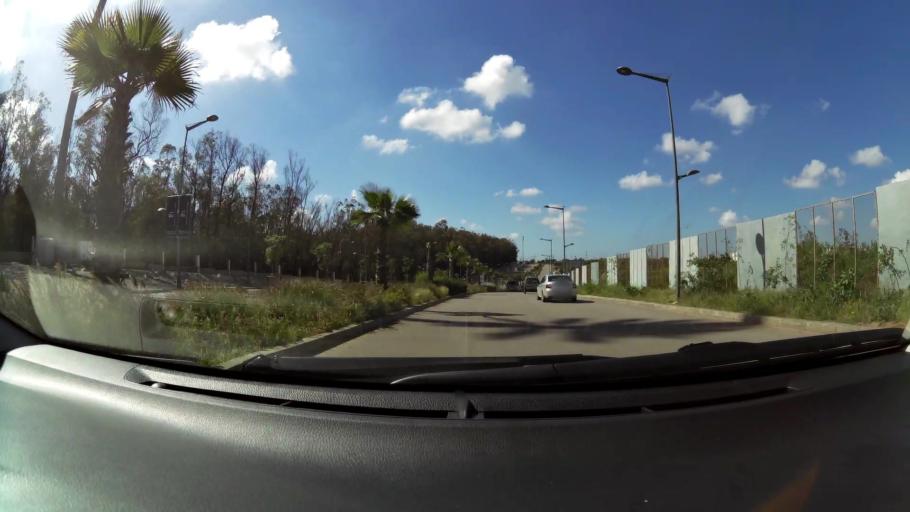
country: MA
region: Grand Casablanca
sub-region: Nouaceur
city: Bouskoura
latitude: 33.4764
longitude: -7.6203
